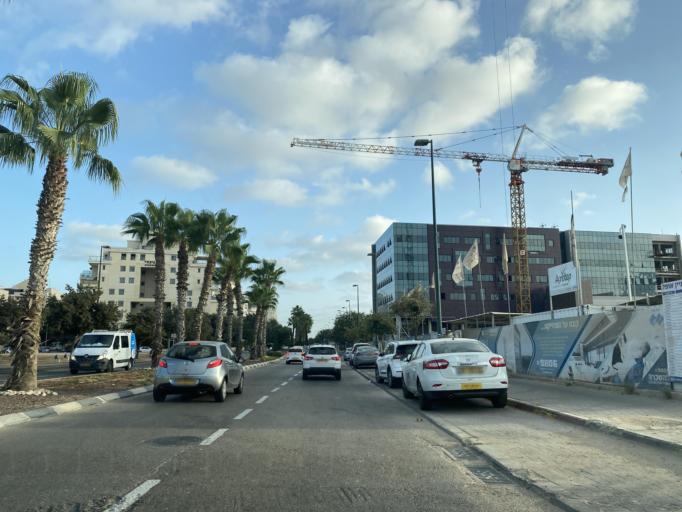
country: IL
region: Central District
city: Netanya
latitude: 32.3115
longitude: 34.8699
